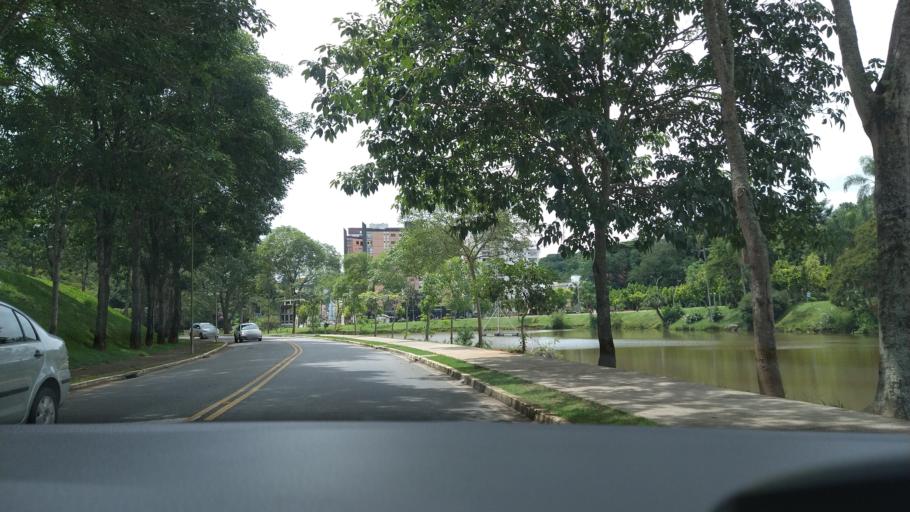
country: BR
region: Minas Gerais
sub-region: Vicosa
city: Vicosa
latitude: -20.7587
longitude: -42.8733
